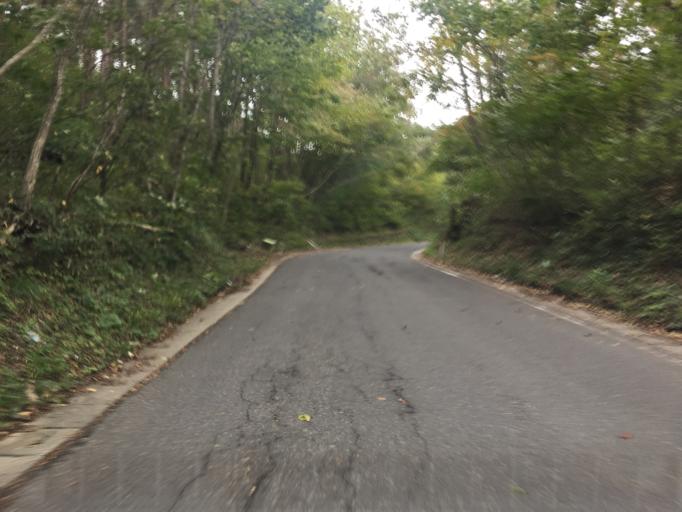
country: JP
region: Miyagi
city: Marumori
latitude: 37.8752
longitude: 140.6987
